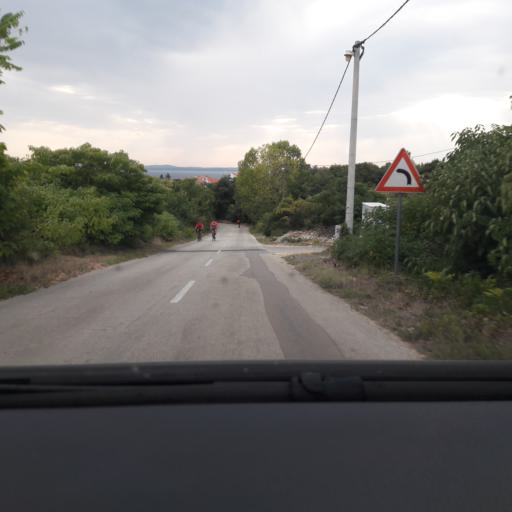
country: HR
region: Zadarska
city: Zadar
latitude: 44.1545
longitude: 15.2080
